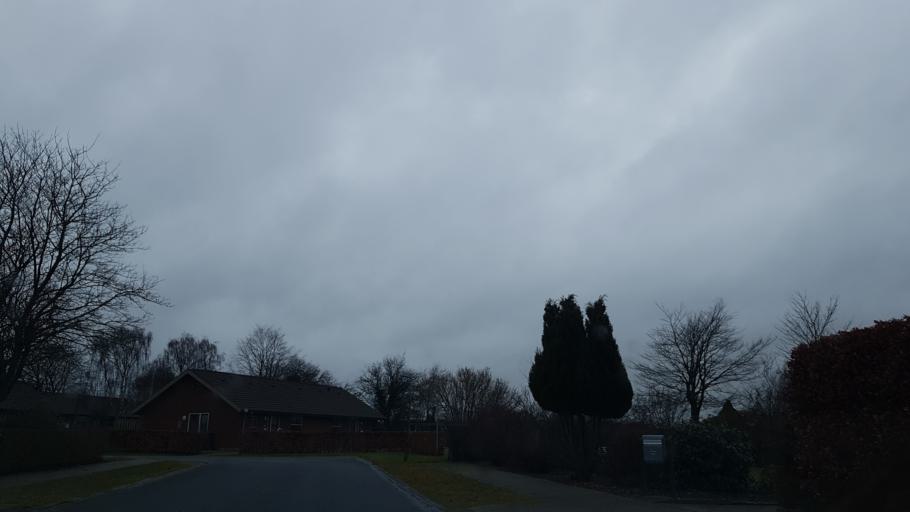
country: DK
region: South Denmark
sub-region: Kolding Kommune
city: Vamdrup
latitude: 55.3586
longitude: 9.1965
